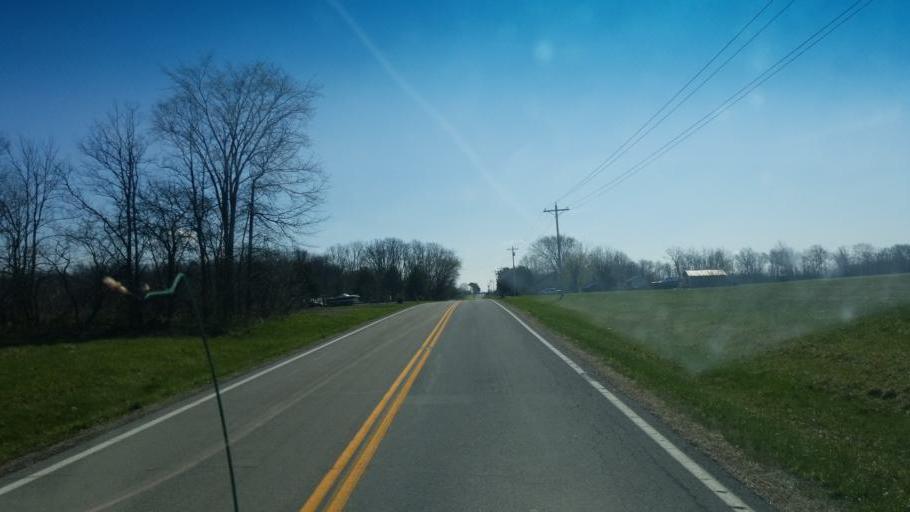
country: US
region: Ohio
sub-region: Hardin County
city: Forest
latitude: 40.7378
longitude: -83.3909
